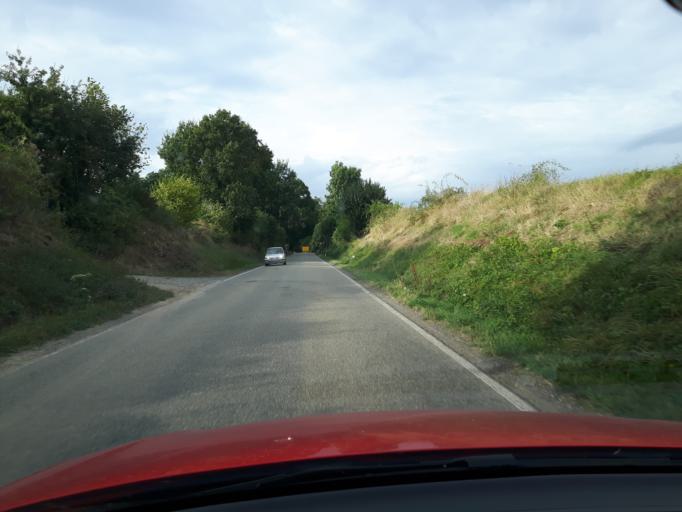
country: DE
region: Baden-Wuerttemberg
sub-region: Regierungsbezirk Stuttgart
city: Nordheim
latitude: 49.0978
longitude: 9.1022
